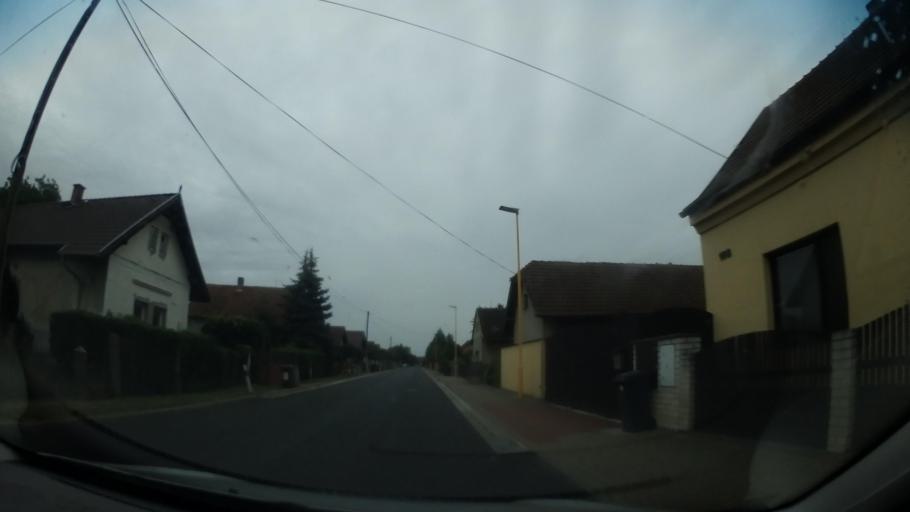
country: CZ
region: Central Bohemia
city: Loucen
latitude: 50.2433
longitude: 15.0229
